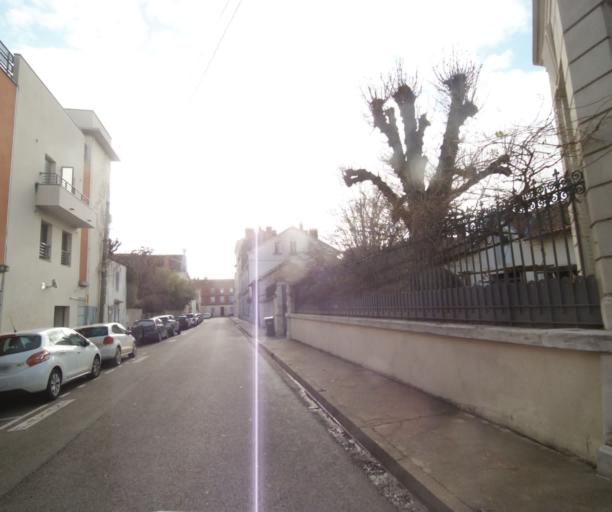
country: FR
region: Rhone-Alpes
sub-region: Departement de la Loire
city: Roanne
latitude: 46.0391
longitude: 4.0667
